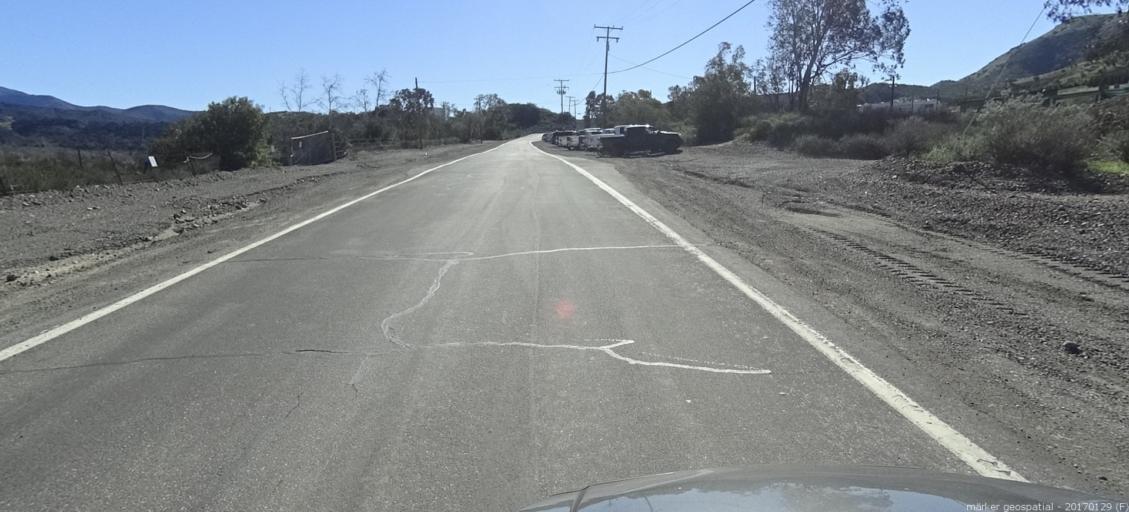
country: US
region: California
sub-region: Orange County
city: Foothill Ranch
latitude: 33.7516
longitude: -117.6731
